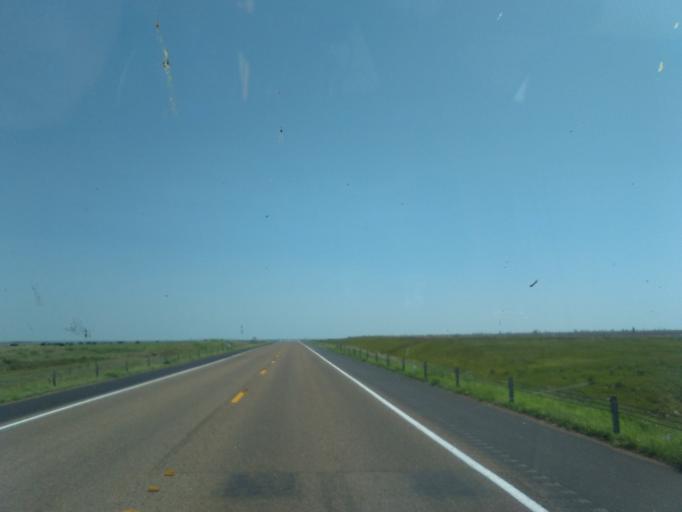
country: US
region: Nebraska
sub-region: Hitchcock County
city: Trenton
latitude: 40.2281
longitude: -100.9220
